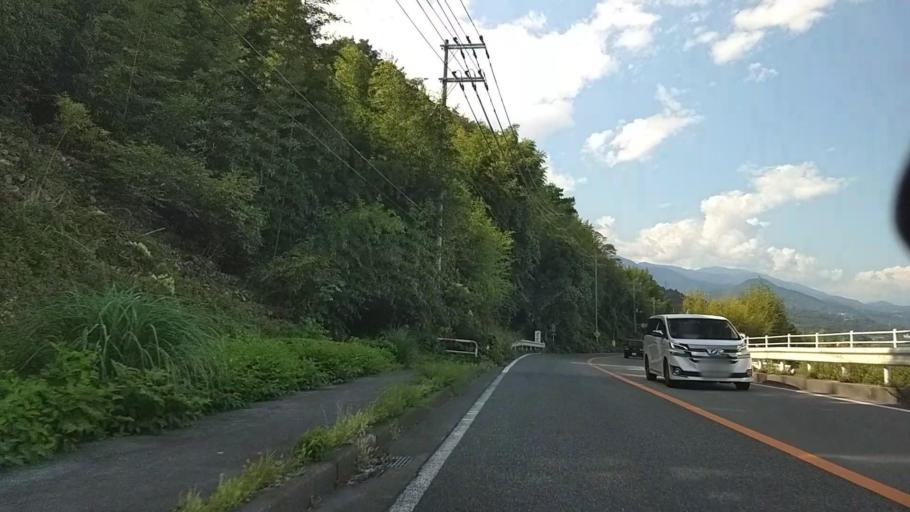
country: JP
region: Shizuoka
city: Fujinomiya
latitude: 35.3880
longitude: 138.4462
